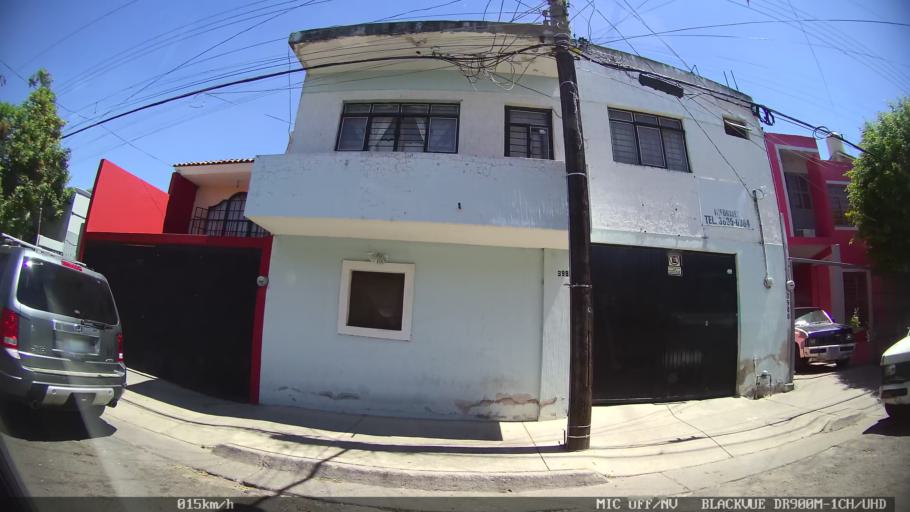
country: MX
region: Jalisco
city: Tlaquepaque
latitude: 20.6775
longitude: -103.2726
